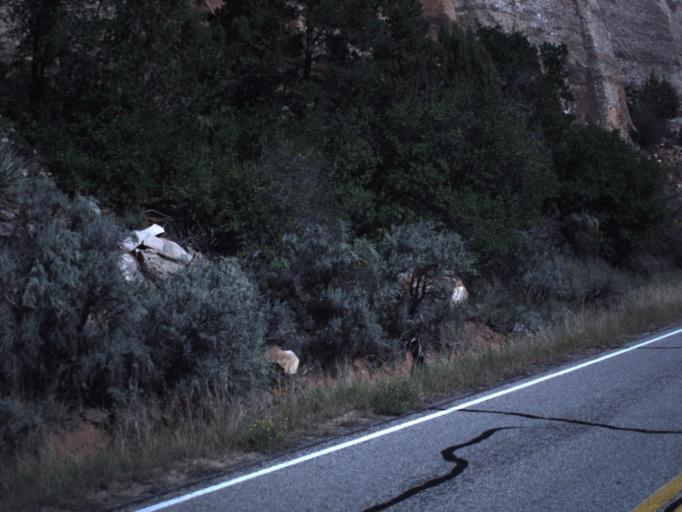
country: US
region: Utah
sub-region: San Juan County
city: Monticello
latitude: 37.9949
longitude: -109.5272
